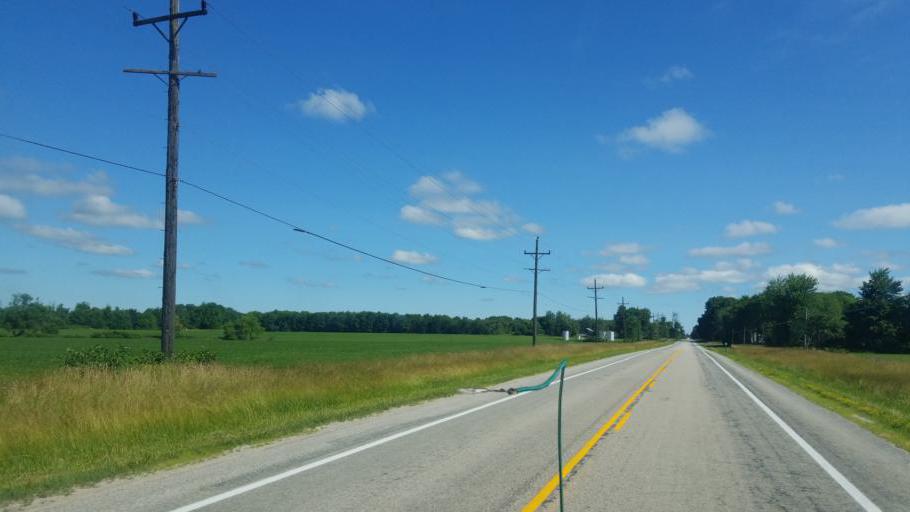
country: US
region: Ohio
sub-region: Ashtabula County
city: Conneaut
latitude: 41.8011
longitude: -80.5721
